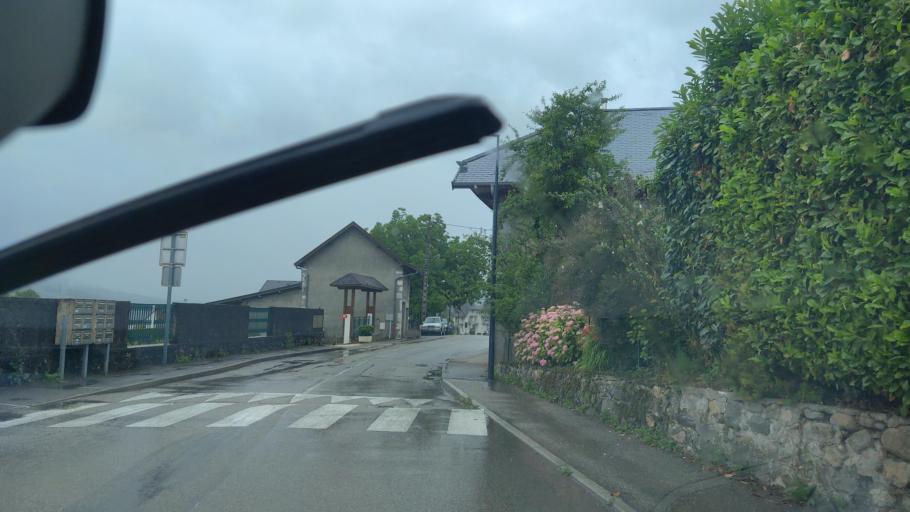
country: FR
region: Rhone-Alpes
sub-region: Departement de la Savoie
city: La Biolle
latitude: 45.7571
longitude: 5.9289
